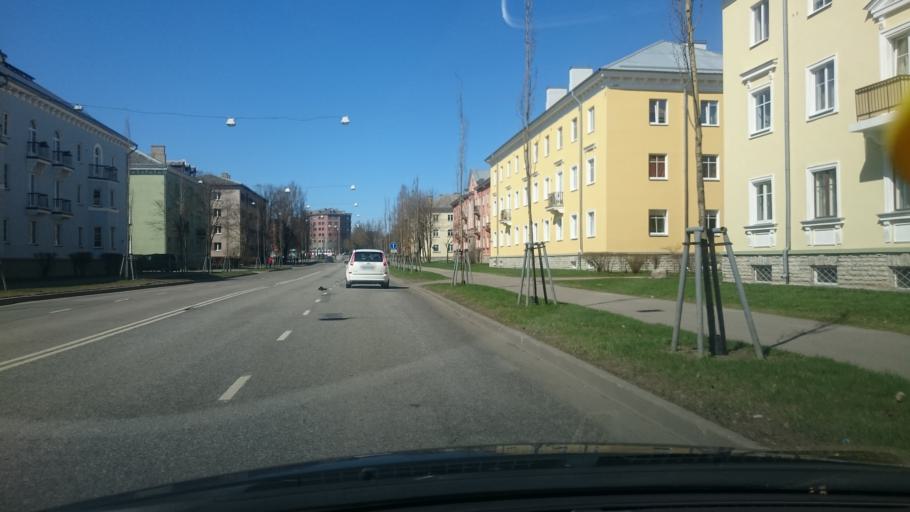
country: EE
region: Harju
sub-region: Tallinna linn
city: Tallinn
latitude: 59.4530
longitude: 24.6926
